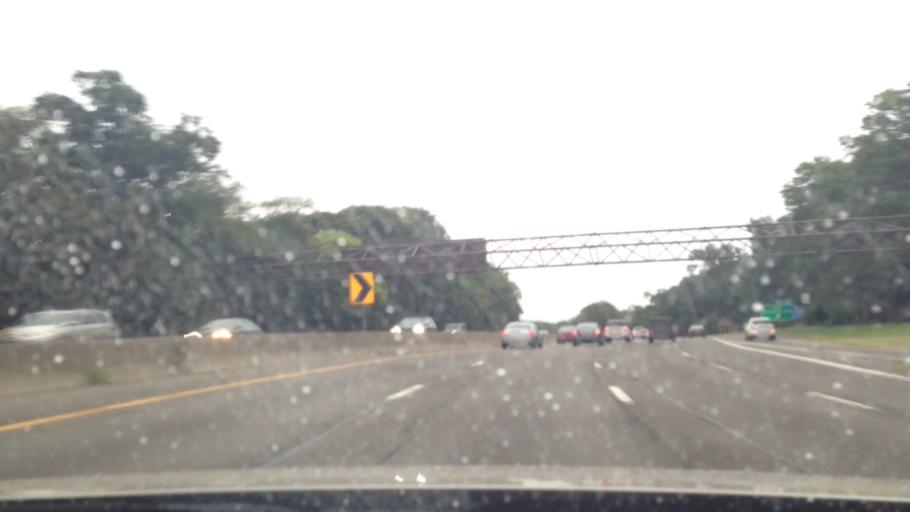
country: US
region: New York
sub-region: Nassau County
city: Elmont
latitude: 40.6935
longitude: -73.7247
